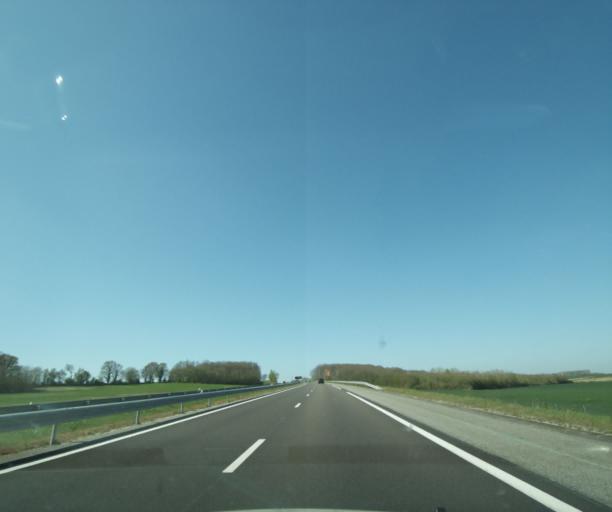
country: FR
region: Bourgogne
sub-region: Departement de la Nievre
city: Neuvy-sur-Loire
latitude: 47.5384
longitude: 2.9013
